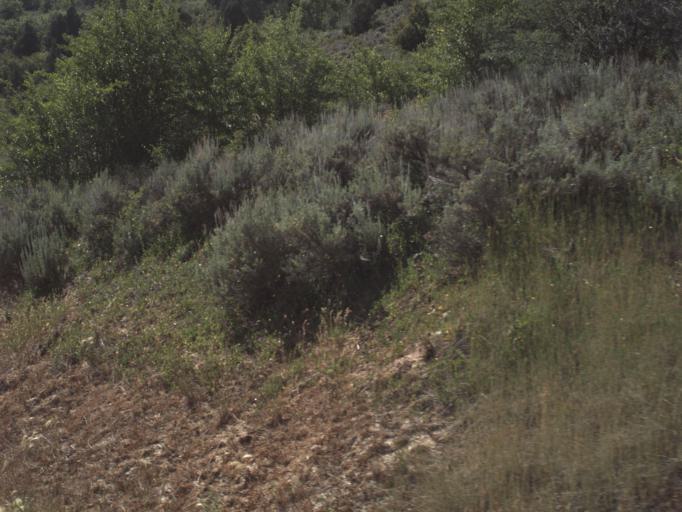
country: US
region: Utah
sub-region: Weber County
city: Wolf Creek
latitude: 41.2838
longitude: -111.6522
